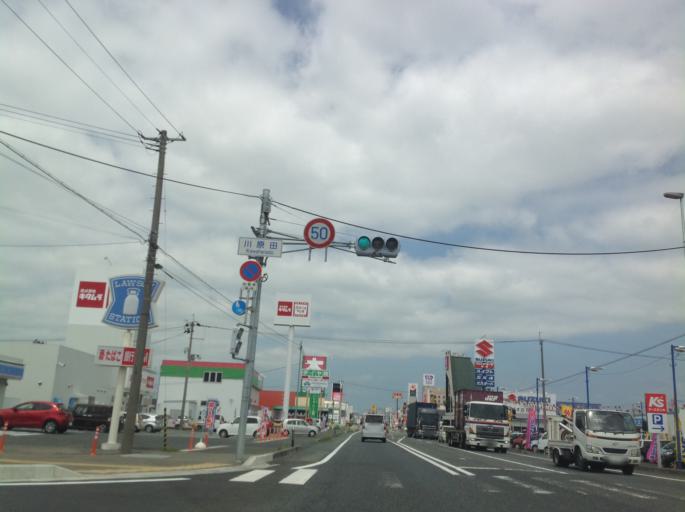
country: JP
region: Iwate
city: Mizusawa
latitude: 39.1443
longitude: 141.1497
